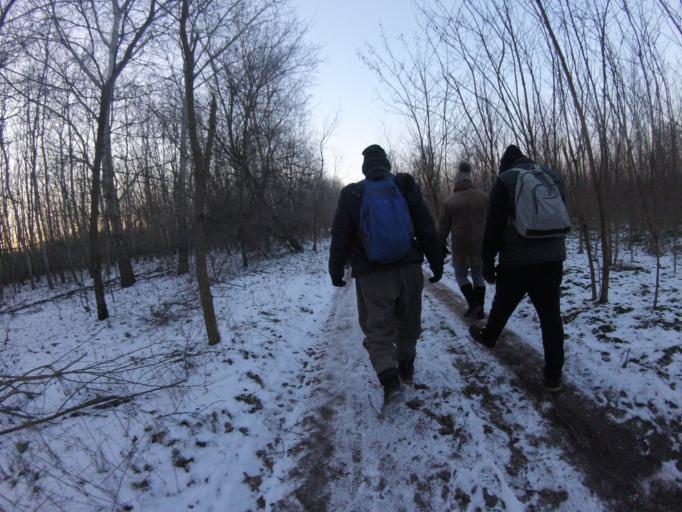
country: HU
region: Budapest
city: Budapest XVII. keruelet
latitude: 47.4529
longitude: 19.2742
